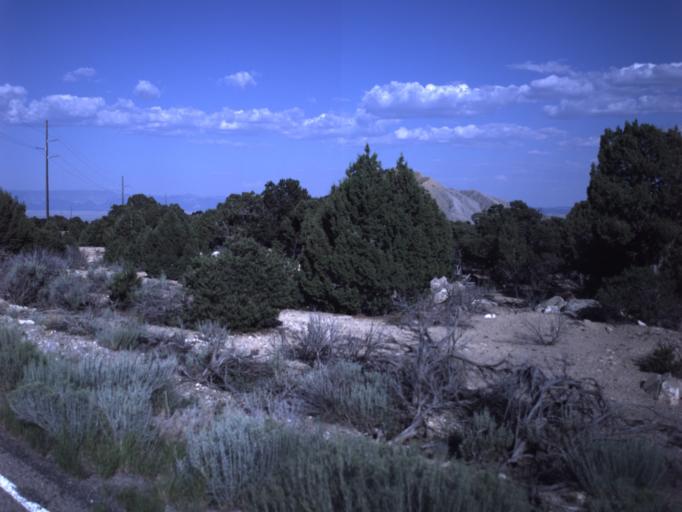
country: US
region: Utah
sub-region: Emery County
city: Huntington
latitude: 39.4859
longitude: -110.9605
